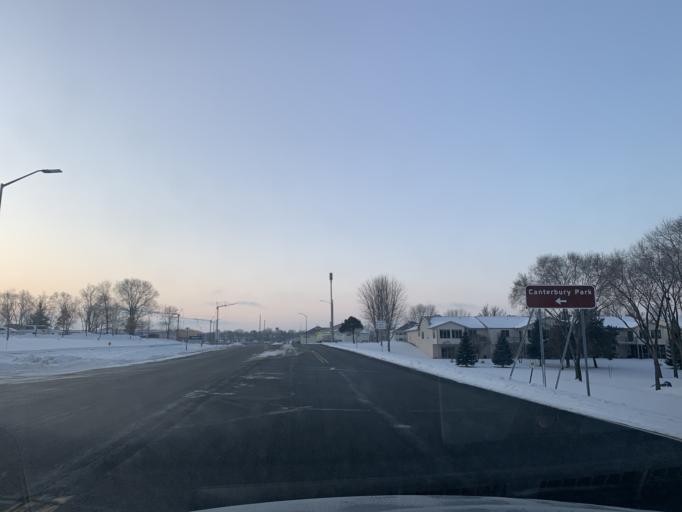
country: US
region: Minnesota
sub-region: Scott County
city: Shakopee
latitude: 44.7949
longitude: -93.4904
